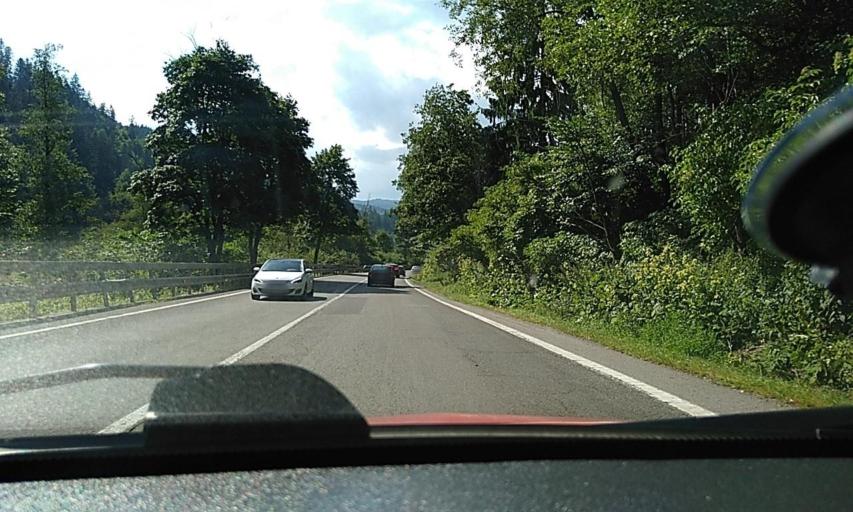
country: RO
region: Brasov
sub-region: Oras Predeal
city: Predeal
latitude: 45.5492
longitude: 25.5934
